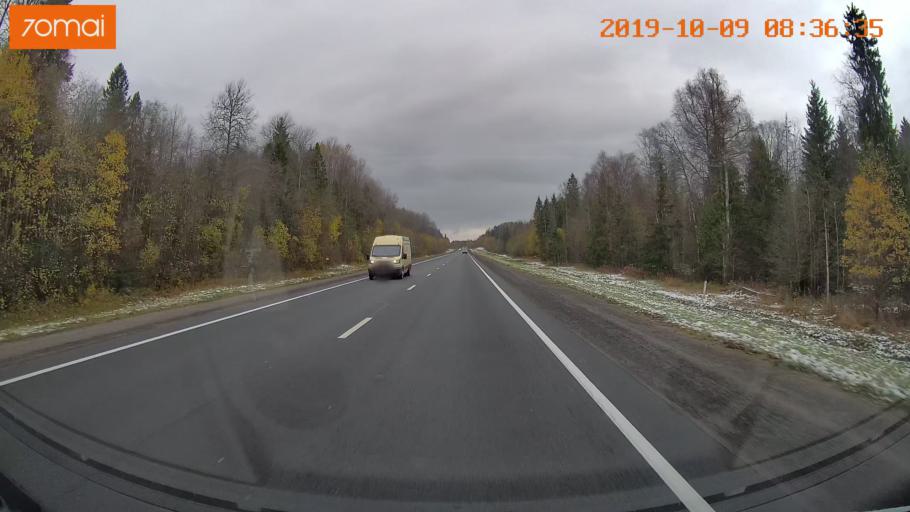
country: RU
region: Vologda
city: Gryazovets
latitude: 58.9288
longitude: 40.1761
